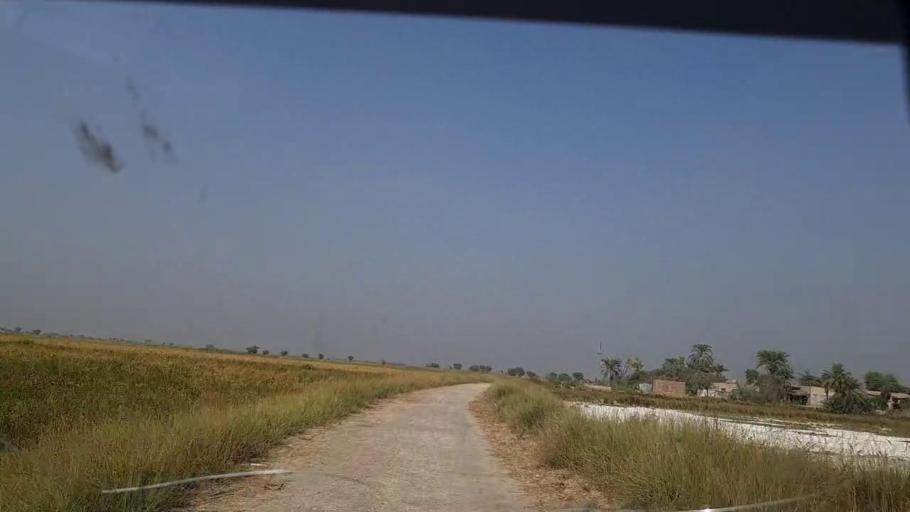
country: PK
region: Sindh
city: Shikarpur
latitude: 28.0939
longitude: 68.6003
